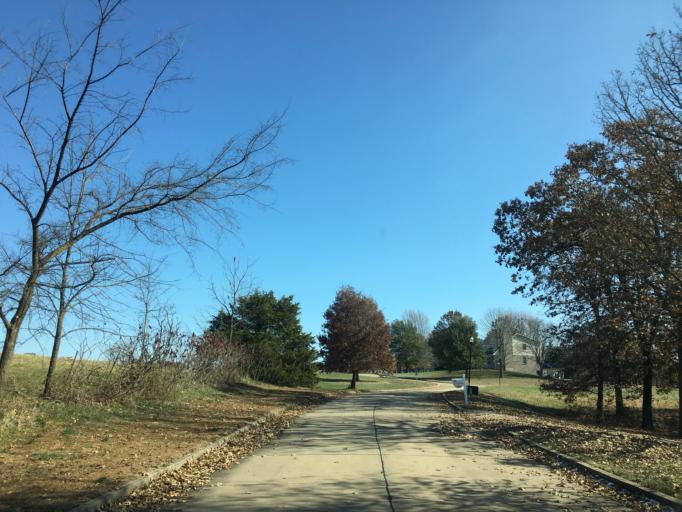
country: US
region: Missouri
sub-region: Cole County
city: Wardsville
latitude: 38.4840
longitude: -92.1804
